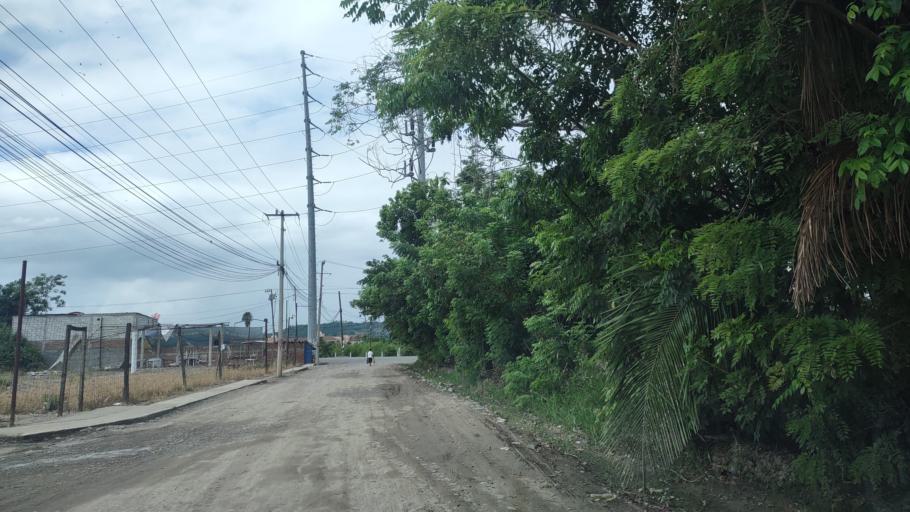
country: MX
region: Veracruz
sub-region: Papantla
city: Residencial Tajin
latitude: 20.5935
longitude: -97.4209
